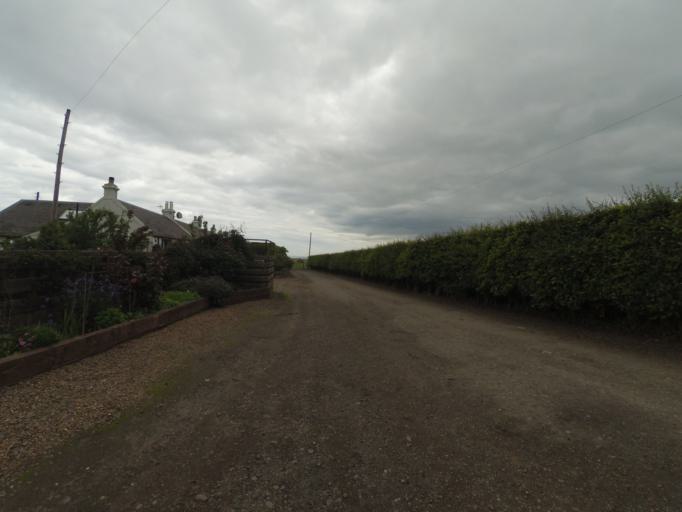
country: GB
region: Scotland
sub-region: East Lothian
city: Prestonpans
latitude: 55.9171
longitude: -2.9983
